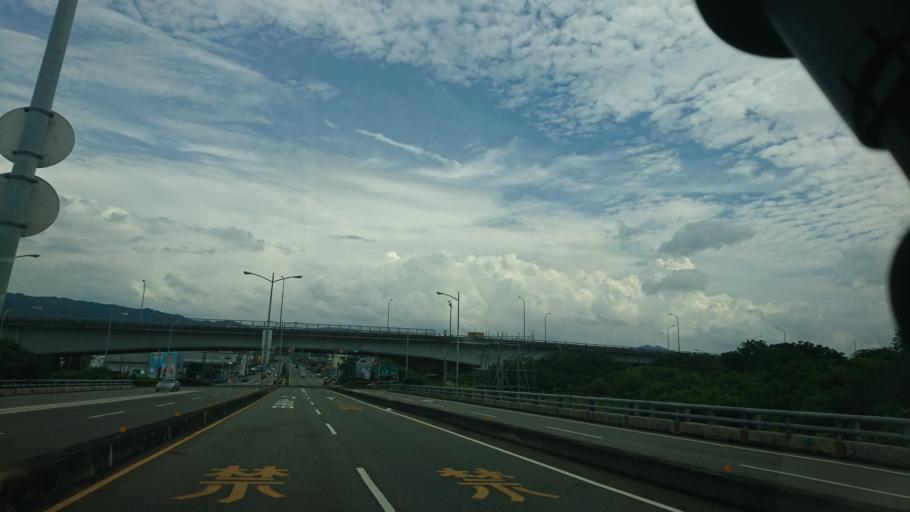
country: TW
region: Taiwan
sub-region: Miaoli
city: Miaoli
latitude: 24.5352
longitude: 120.8162
